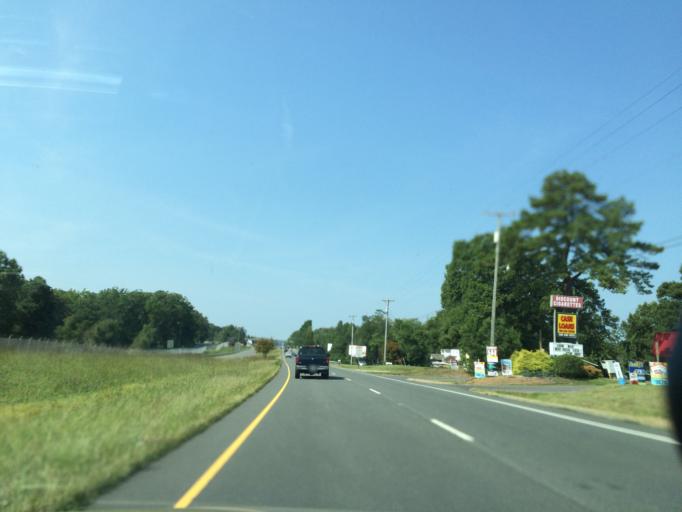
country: US
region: Virginia
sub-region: King George County
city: Dahlgren
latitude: 38.3553
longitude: -77.0425
